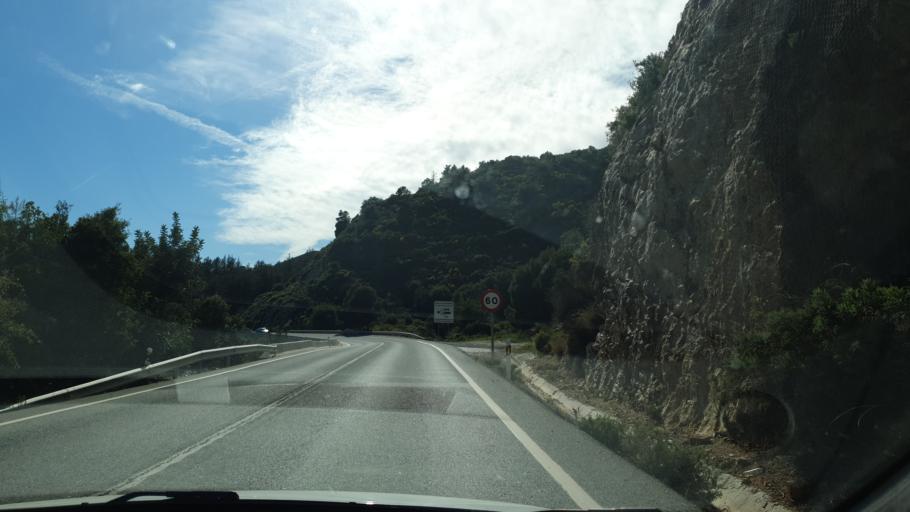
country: ES
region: Andalusia
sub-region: Provincia de Malaga
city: Ojen
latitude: 36.5761
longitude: -4.8562
